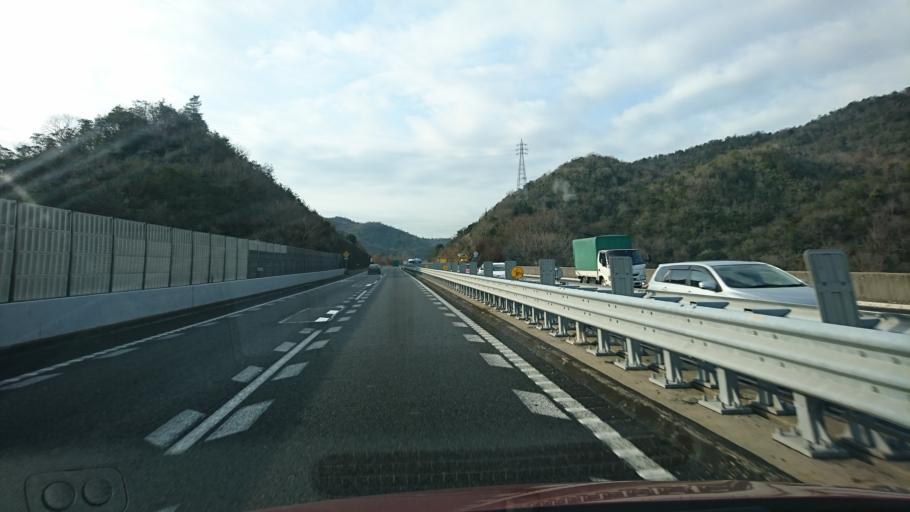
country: JP
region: Hyogo
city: Aioi
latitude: 34.8007
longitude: 134.4362
